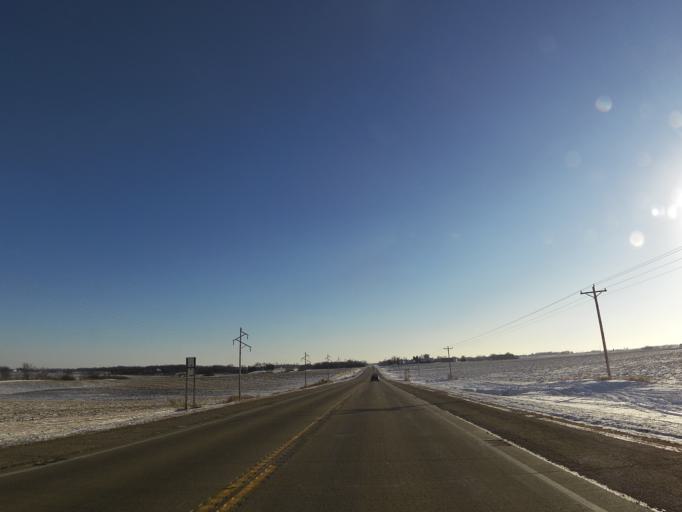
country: US
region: Minnesota
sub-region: Le Sueur County
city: New Prague
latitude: 44.5135
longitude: -93.5857
